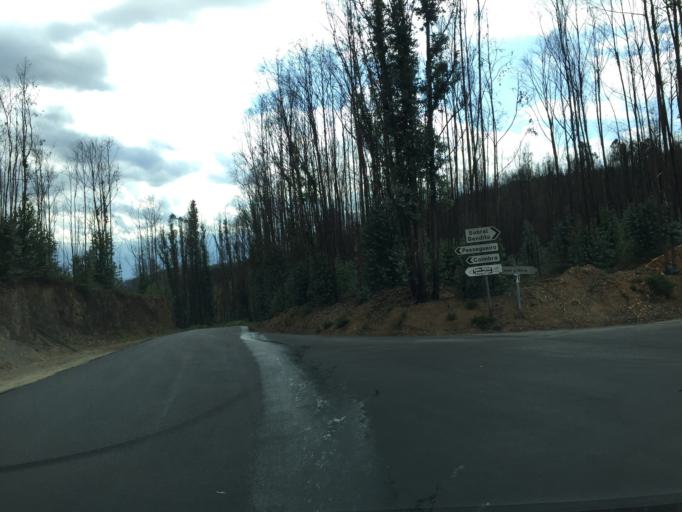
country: PT
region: Coimbra
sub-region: Pampilhosa da Serra
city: Pampilhosa da Serra
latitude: 40.0592
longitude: -8.0091
